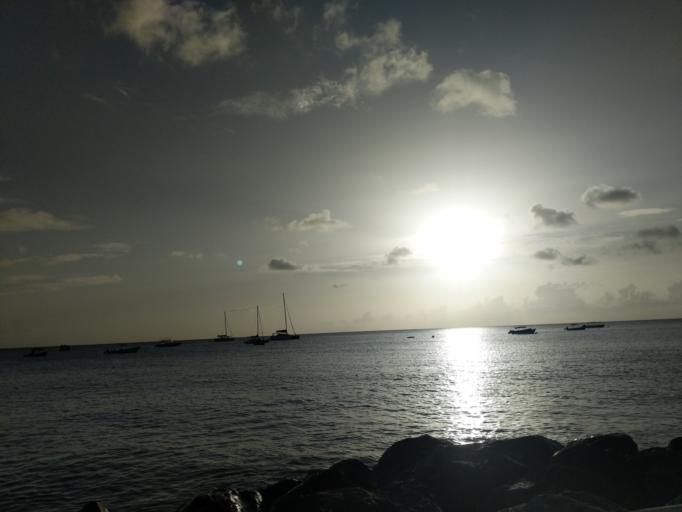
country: BB
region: Saint James
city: Holetown
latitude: 13.1856
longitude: -59.6387
